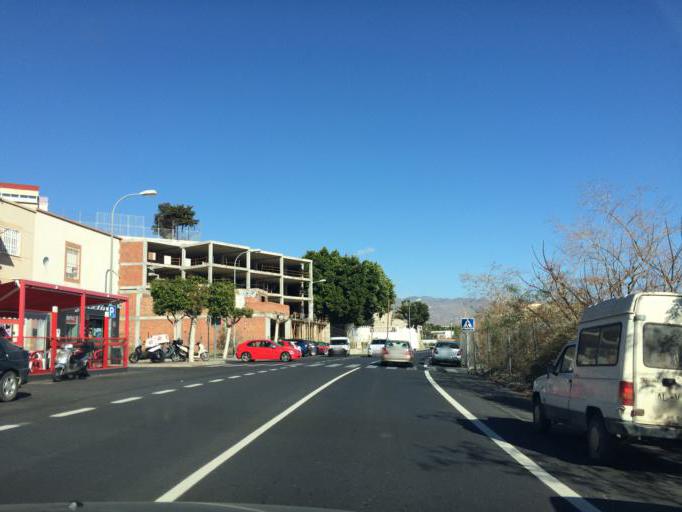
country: ES
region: Andalusia
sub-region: Provincia de Almeria
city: Huercal de Almeria
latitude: 36.8789
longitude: -2.4381
